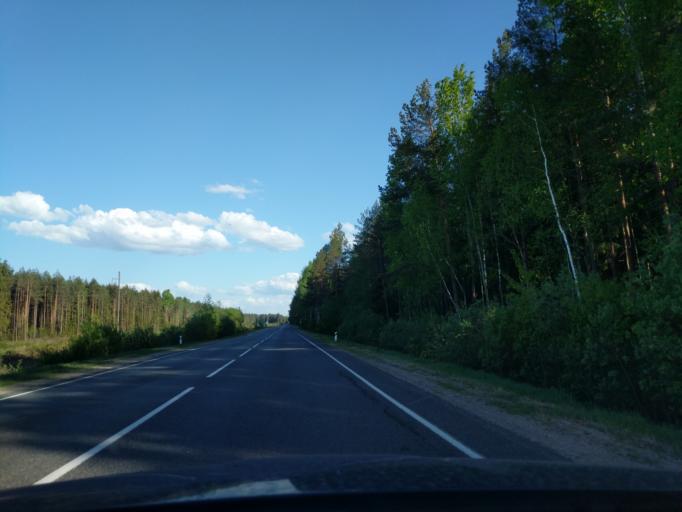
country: BY
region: Minsk
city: Kryvichy
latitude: 54.7511
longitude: 27.1117
